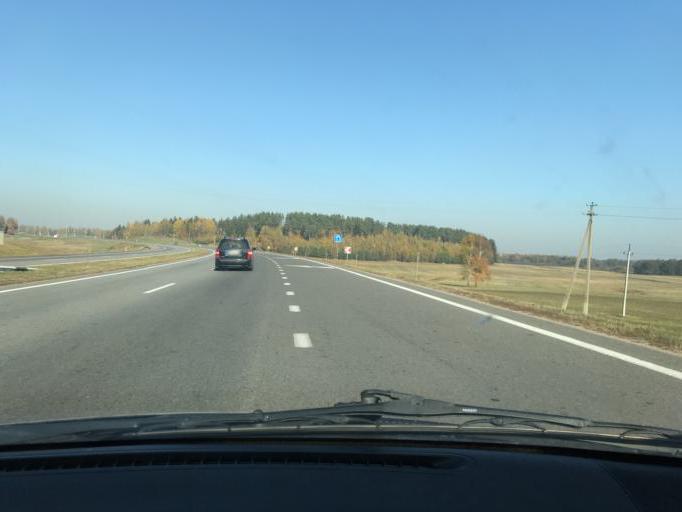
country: BY
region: Minsk
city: Samakhvalavichy
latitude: 53.6972
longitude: 27.5255
